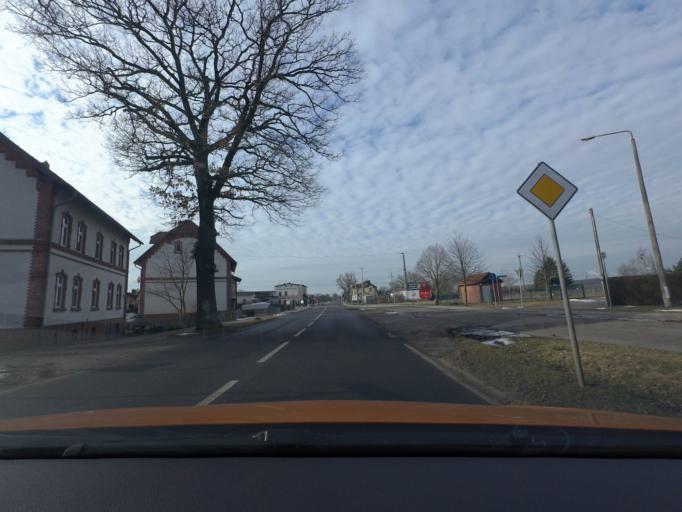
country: DE
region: Brandenburg
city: Gransee
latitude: 52.8988
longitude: 13.1901
